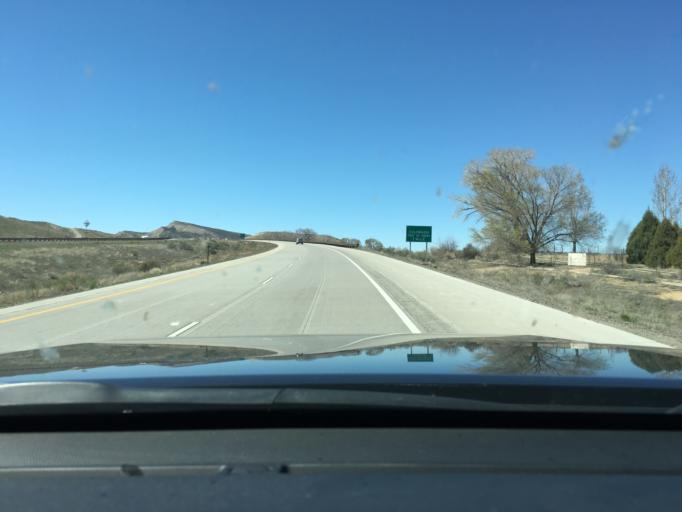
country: US
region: Colorado
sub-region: Mesa County
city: Loma
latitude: 39.1768
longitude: -108.8026
